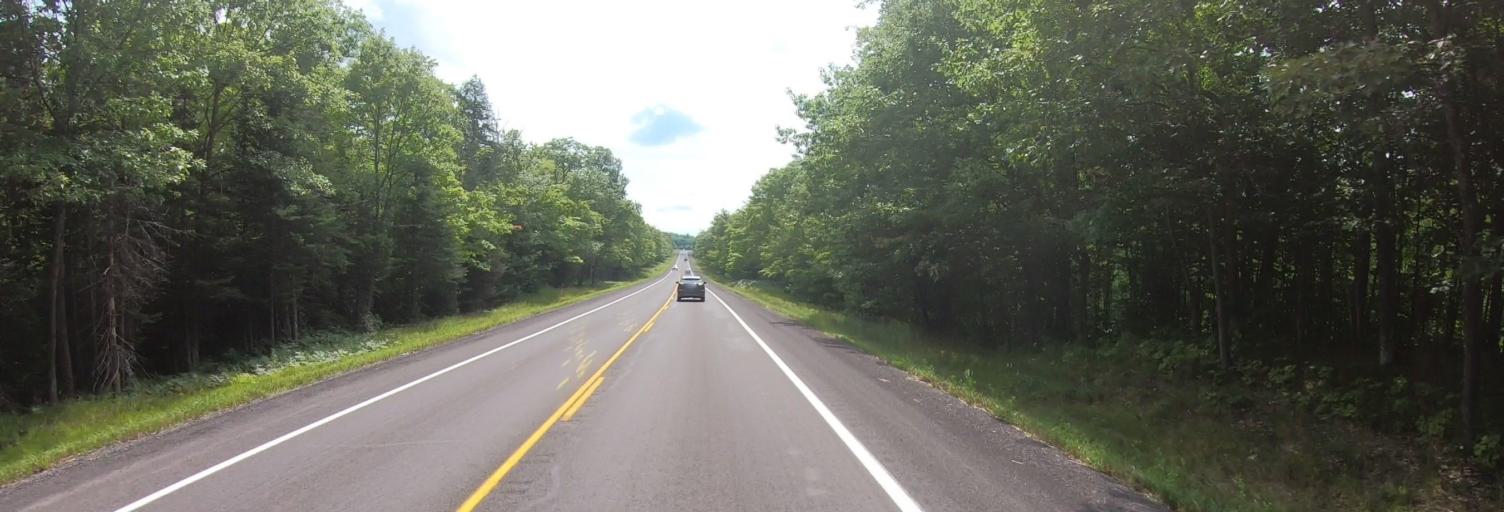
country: US
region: Michigan
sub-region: Houghton County
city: Hancock
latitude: 47.0177
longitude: -88.7424
